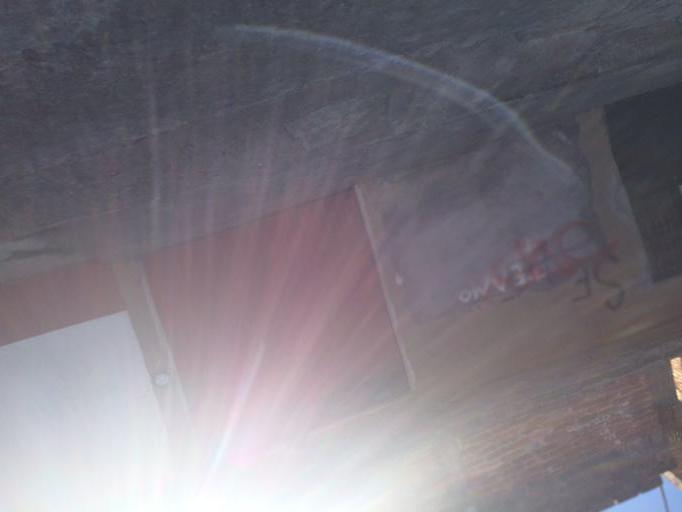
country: MX
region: Michoacan
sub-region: Patzcuaro
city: Colonia Vista Bella (Lomas del Peaje)
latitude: 19.4986
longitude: -101.6026
